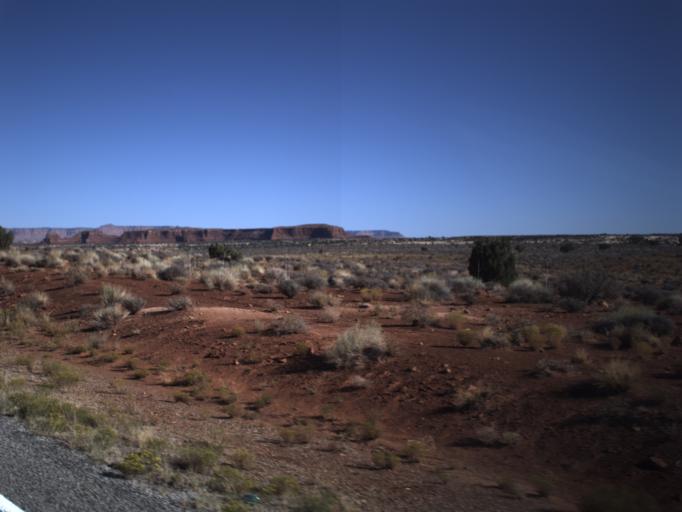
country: US
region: Utah
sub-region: San Juan County
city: Blanding
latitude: 37.7774
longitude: -110.2901
